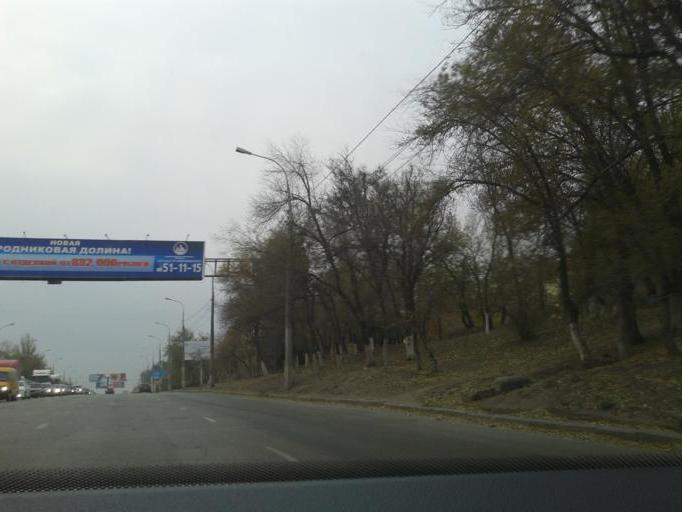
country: RU
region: Volgograd
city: Volgograd
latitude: 48.6783
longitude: 44.4449
